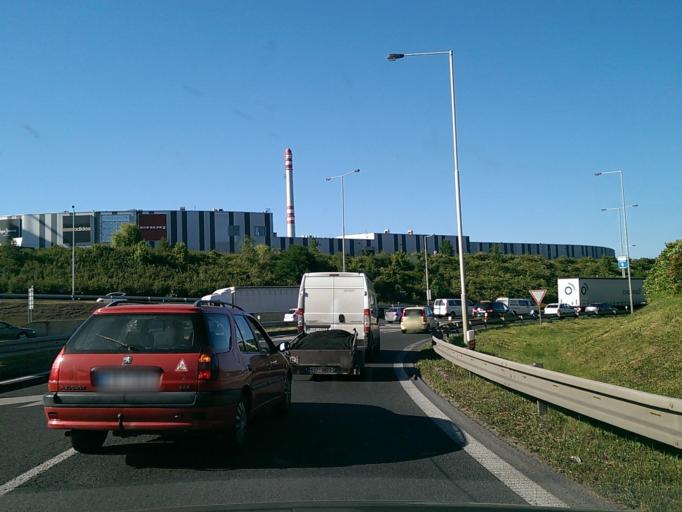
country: CZ
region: Praha
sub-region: Praha 14
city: Hostavice
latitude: 50.0724
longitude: 14.5397
